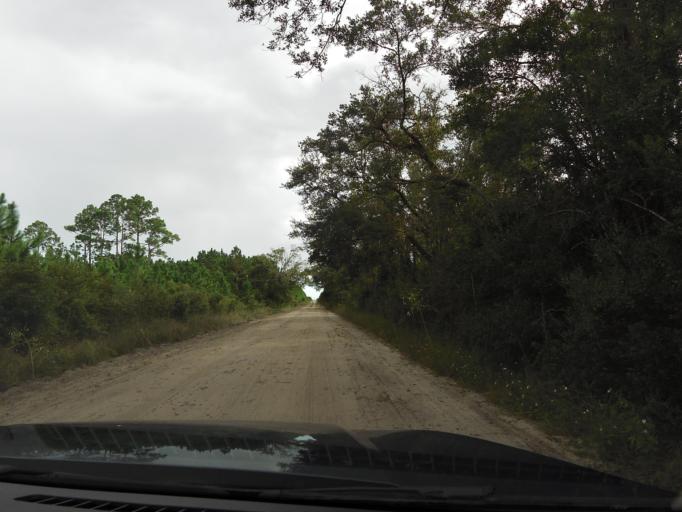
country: US
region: Florida
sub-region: Flagler County
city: Bunnell
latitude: 29.5687
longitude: -81.3372
